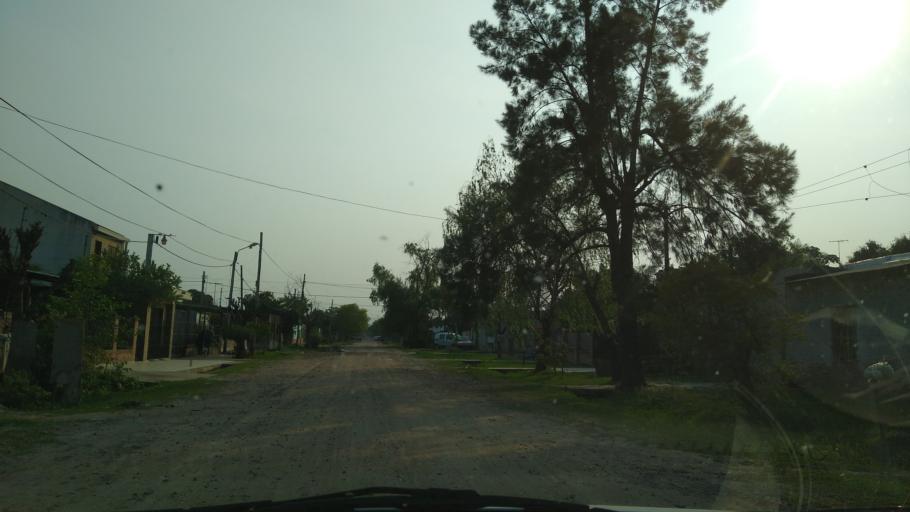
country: AR
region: Chaco
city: Resistencia
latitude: -27.4865
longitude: -58.9723
